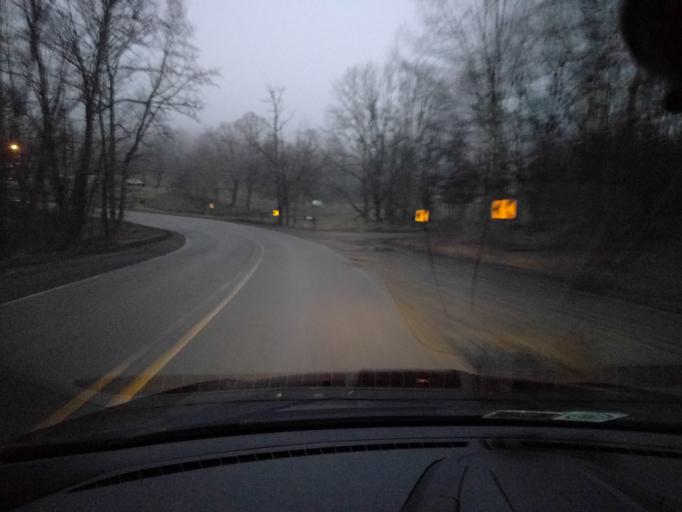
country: US
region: West Virginia
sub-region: Greenbrier County
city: Rainelle
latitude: 37.9684
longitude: -80.8071
